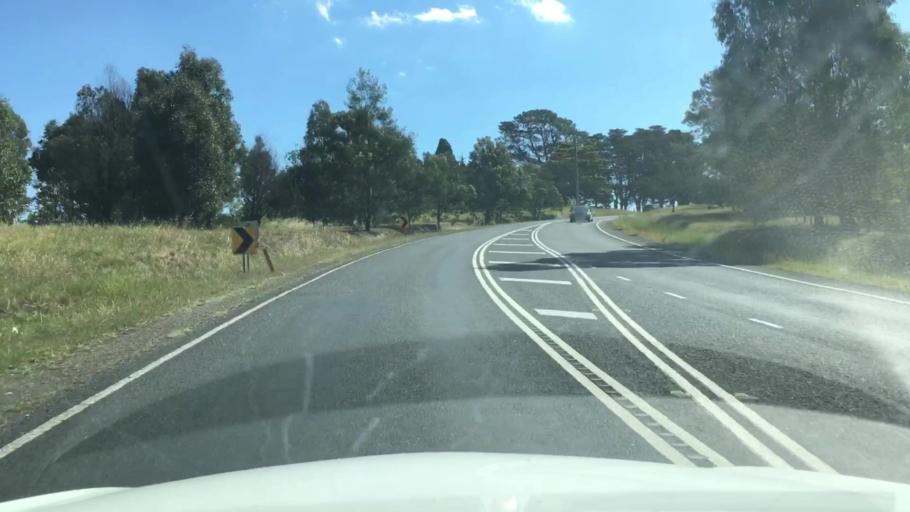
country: AU
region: Victoria
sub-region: Nillumbik
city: North Warrandyte
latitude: -37.6893
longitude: 145.2336
